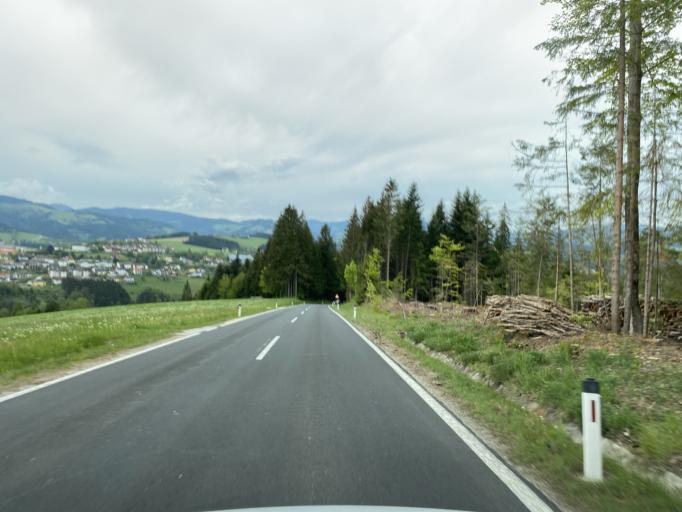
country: AT
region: Styria
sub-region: Politischer Bezirk Weiz
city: Birkfeld
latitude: 47.3475
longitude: 15.7080
